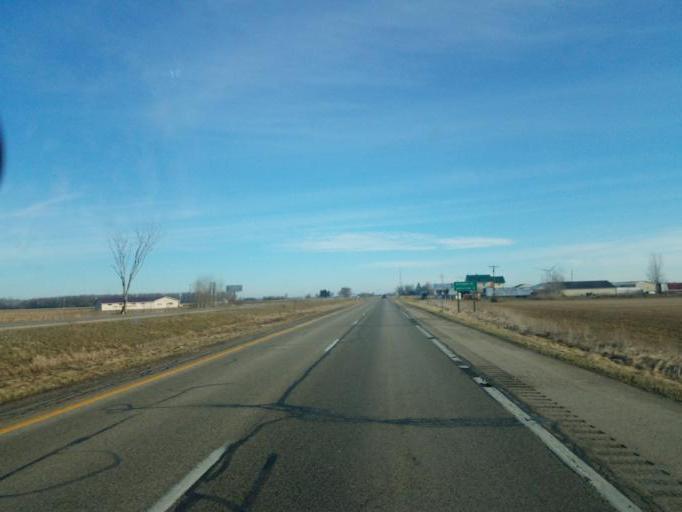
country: US
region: Michigan
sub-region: Gratiot County
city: Ithaca
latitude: 43.2455
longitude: -84.5631
